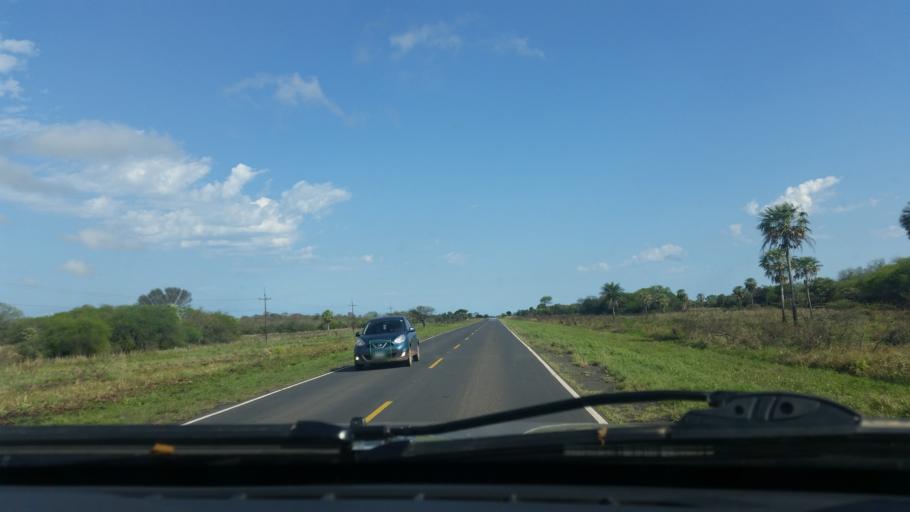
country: PY
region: Presidente Hayes
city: Benjamin Aceval
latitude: -24.9050
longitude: -57.6489
